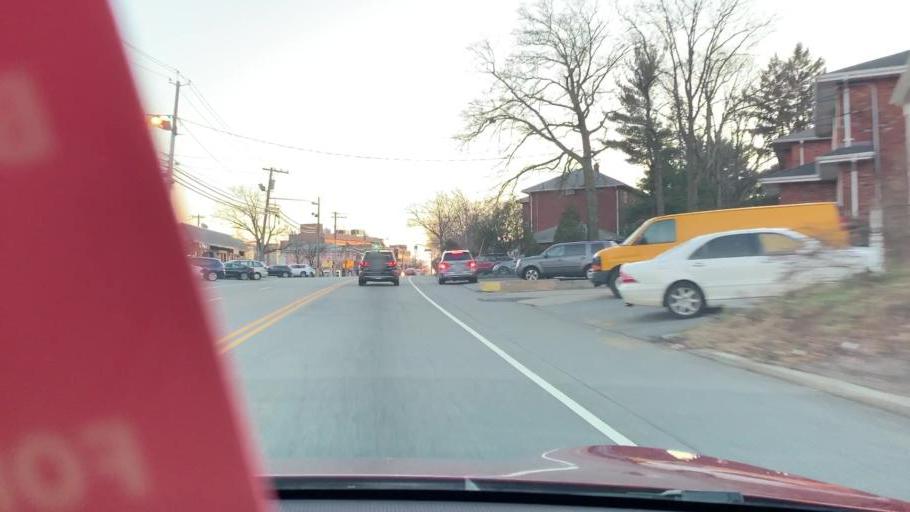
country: US
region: New Jersey
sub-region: Bergen County
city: Palisades Park
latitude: 40.8483
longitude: -73.9850
